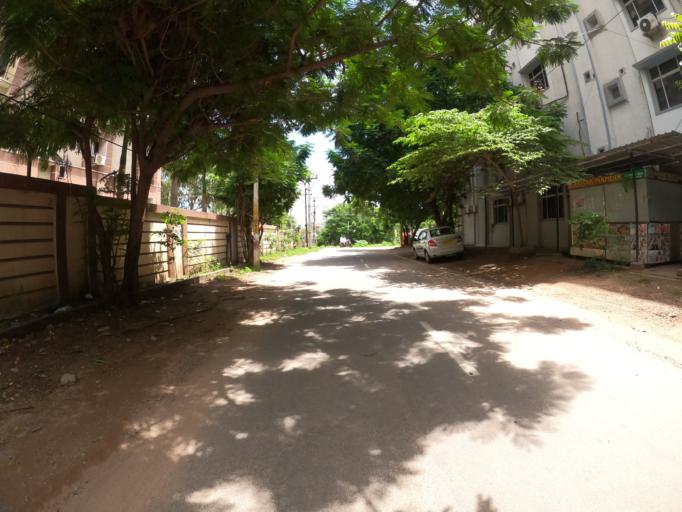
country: IN
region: Telangana
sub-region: Hyderabad
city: Hyderabad
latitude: 17.3708
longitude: 78.4228
